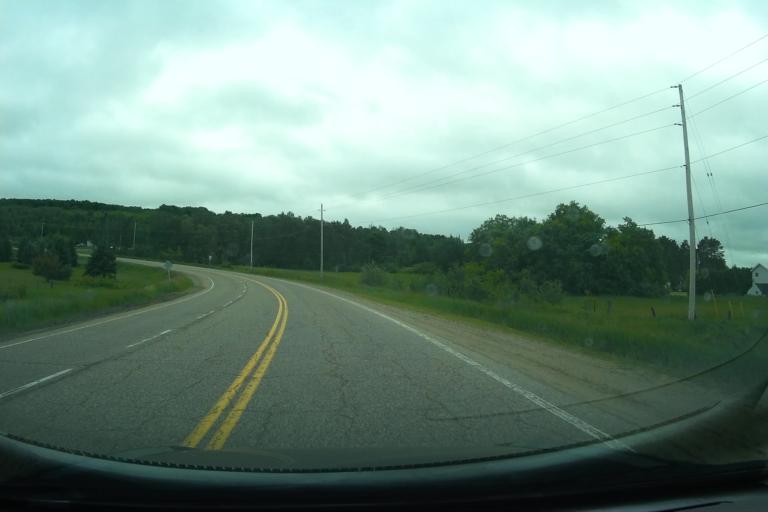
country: CA
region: Ontario
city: Pembroke
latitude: 45.4621
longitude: -77.2930
